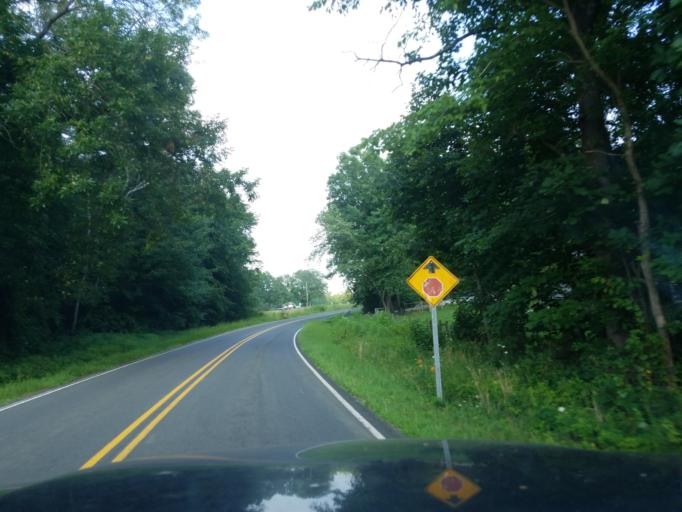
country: US
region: North Carolina
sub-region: Granville County
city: Butner
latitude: 36.2013
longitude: -78.8482
